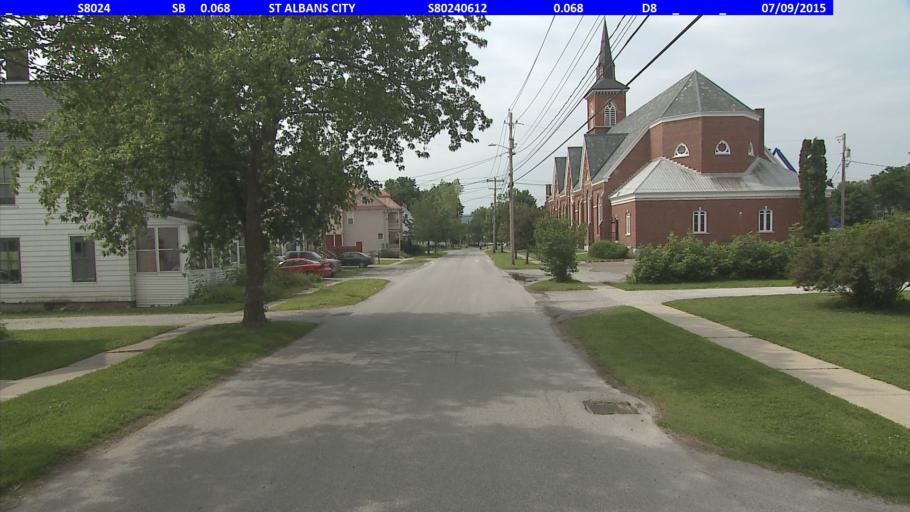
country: US
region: Vermont
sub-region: Franklin County
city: Saint Albans
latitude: 44.8122
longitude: -73.0924
